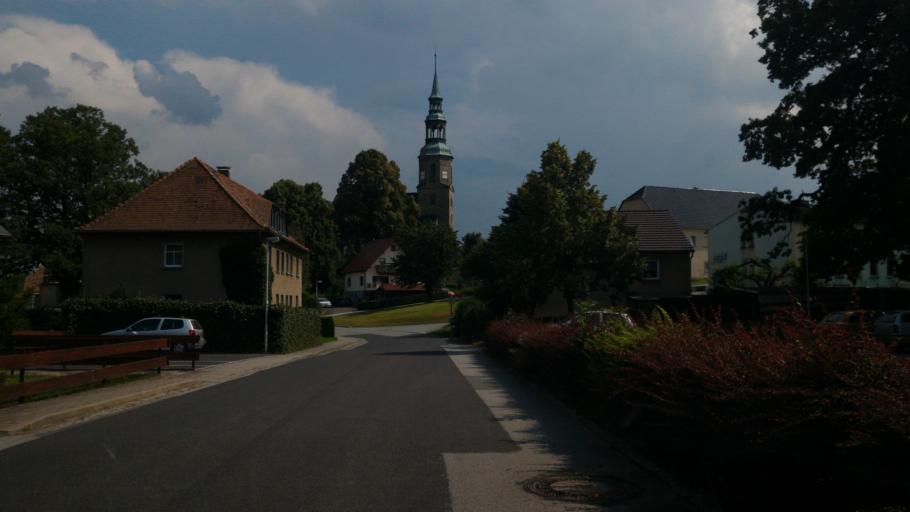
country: DE
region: Saxony
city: Hirschfelde
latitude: 50.9440
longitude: 14.8364
